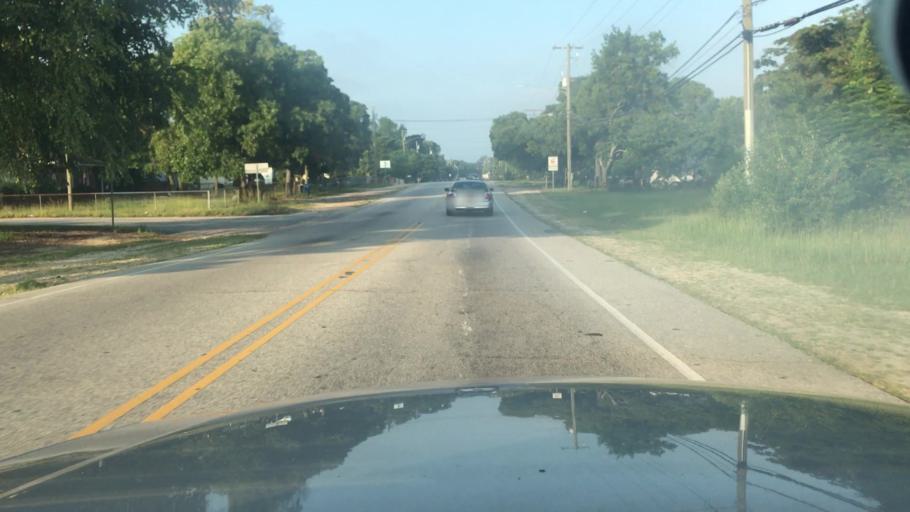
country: US
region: North Carolina
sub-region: Cumberland County
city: Spring Lake
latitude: 35.1136
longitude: -78.9316
